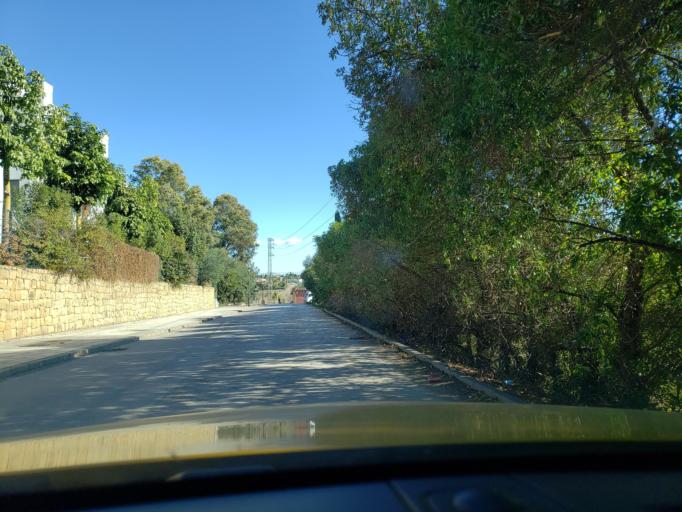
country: ES
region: Andalusia
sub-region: Provincia de Malaga
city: Benahavis
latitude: 36.4851
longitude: -5.0167
